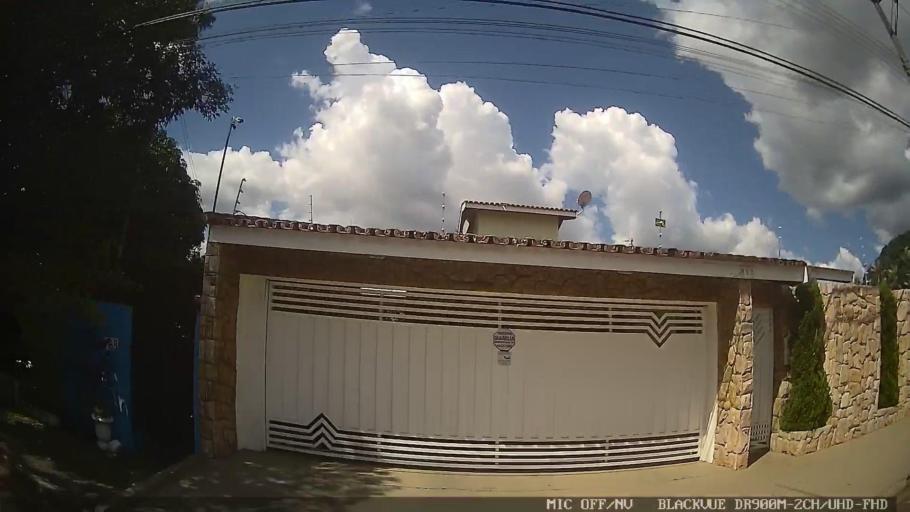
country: BR
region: Sao Paulo
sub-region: Atibaia
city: Atibaia
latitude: -23.1411
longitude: -46.5641
